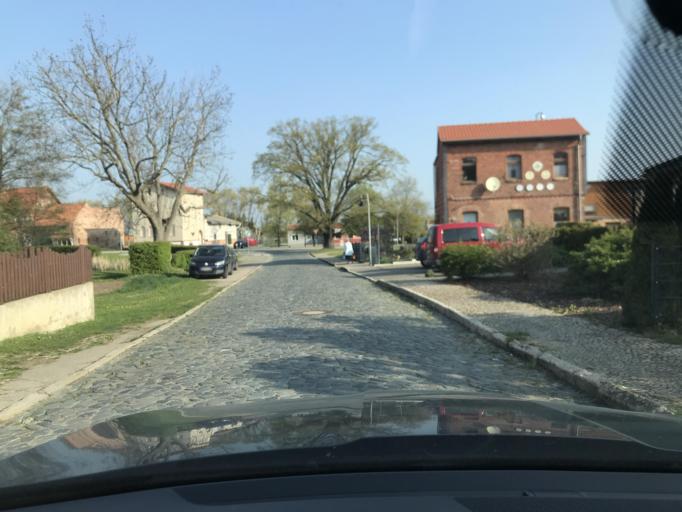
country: DE
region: Saxony-Anhalt
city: Huy-Neinstedt
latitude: 51.9775
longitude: 10.9804
